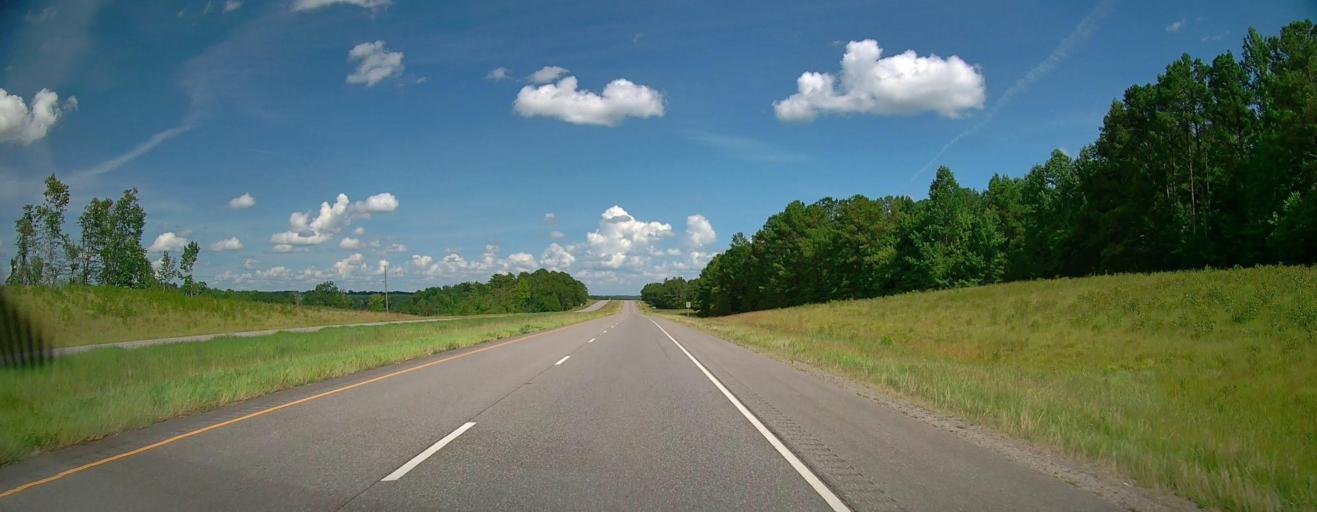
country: US
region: Alabama
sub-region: Pickens County
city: Reform
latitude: 33.3947
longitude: -88.0530
